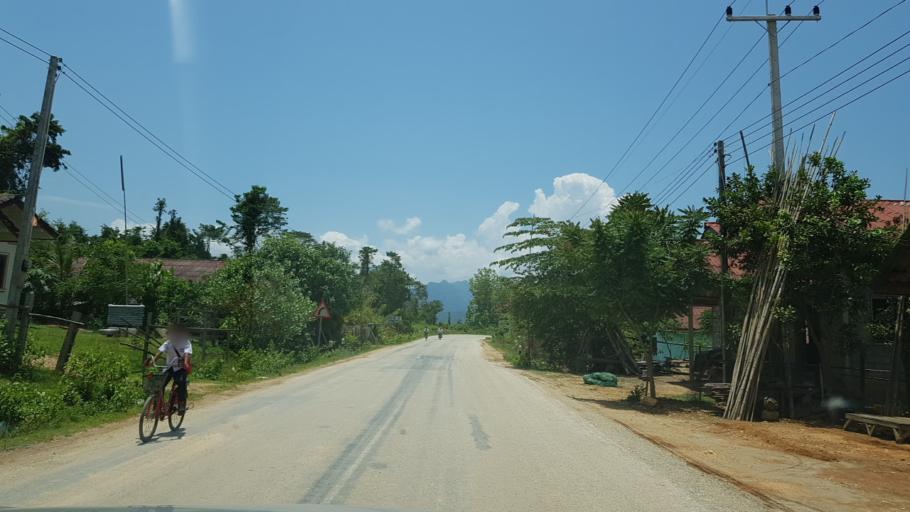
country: LA
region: Vientiane
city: Muang Kasi
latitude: 19.2625
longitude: 102.2323
